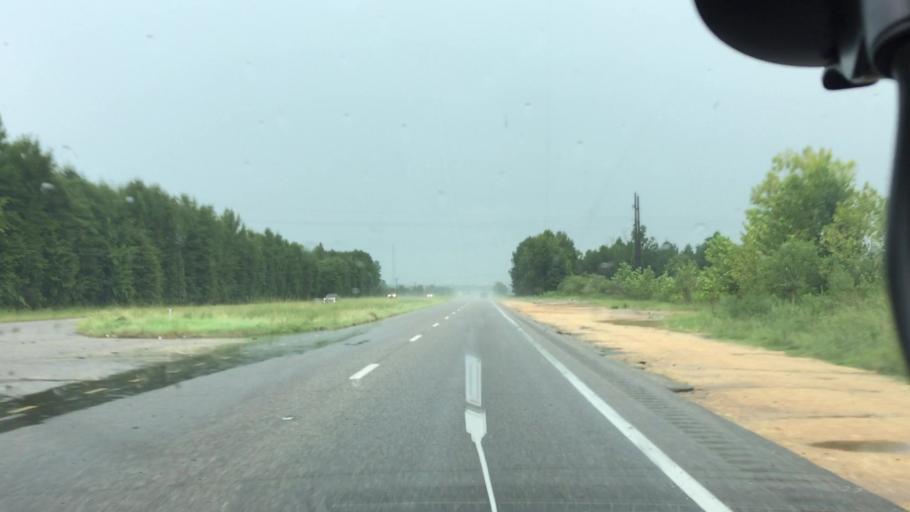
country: US
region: Alabama
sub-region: Montgomery County
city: Pike Road
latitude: 32.2387
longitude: -86.1297
